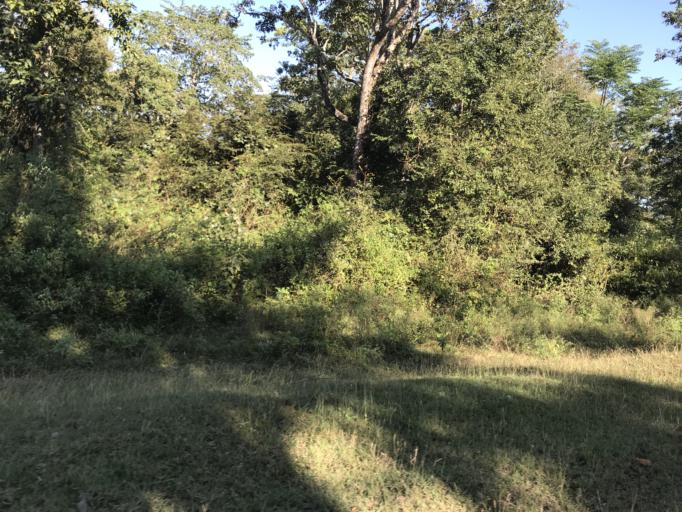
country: IN
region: Karnataka
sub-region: Mysore
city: Heggadadevankote
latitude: 11.9745
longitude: 76.2416
